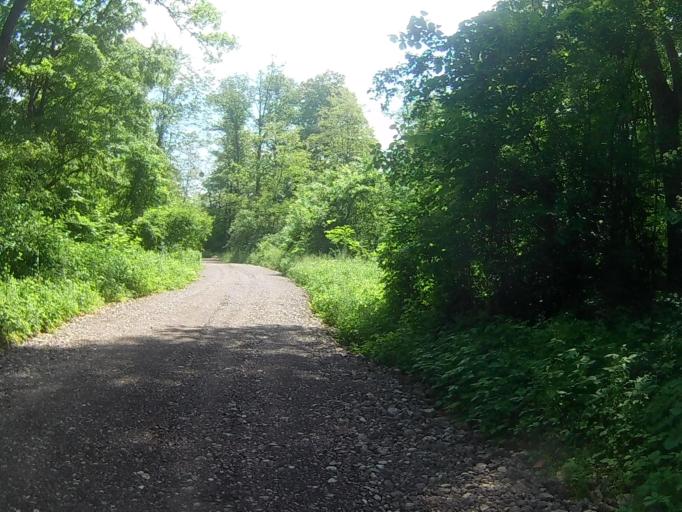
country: SI
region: Starse
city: Starse
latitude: 46.4811
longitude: 15.7600
